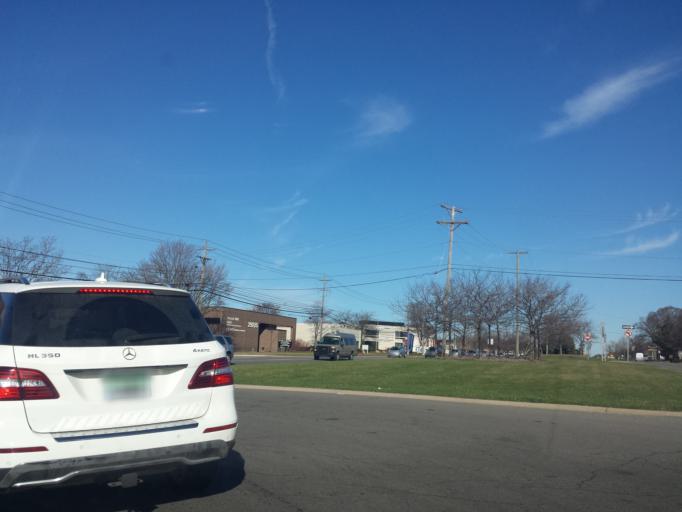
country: US
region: Michigan
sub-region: Oakland County
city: Franklin
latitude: 42.5029
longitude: -83.3121
